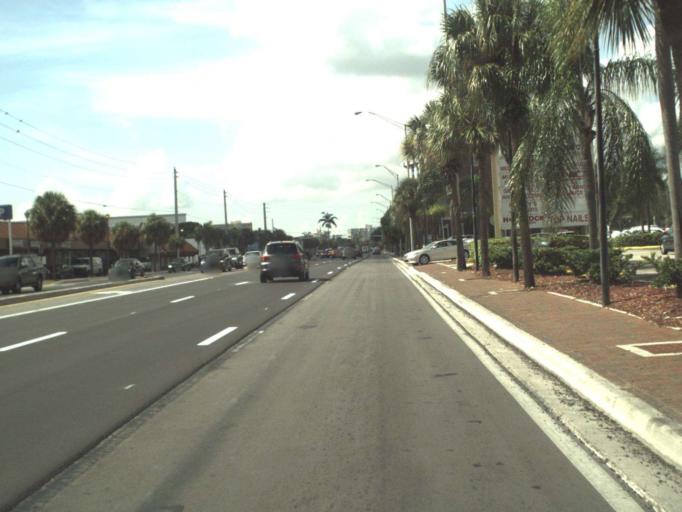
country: US
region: Florida
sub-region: Miami-Dade County
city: Biscayne Park
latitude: 25.8954
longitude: -80.1621
